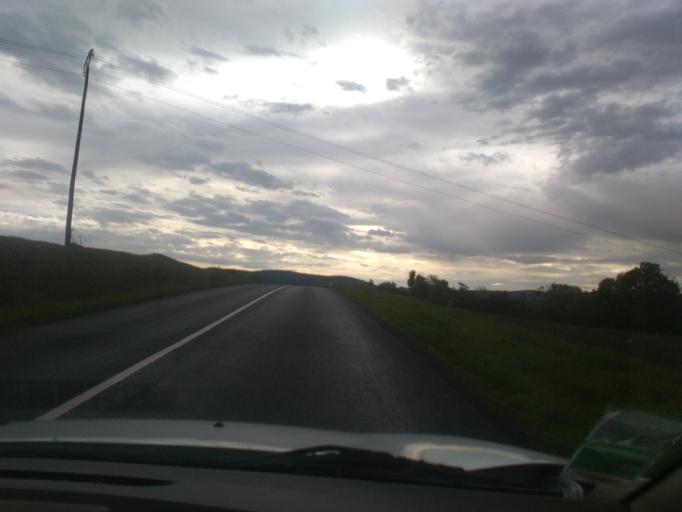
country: FR
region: Lorraine
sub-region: Departement des Vosges
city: Bruyeres
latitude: 48.1899
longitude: 6.7418
